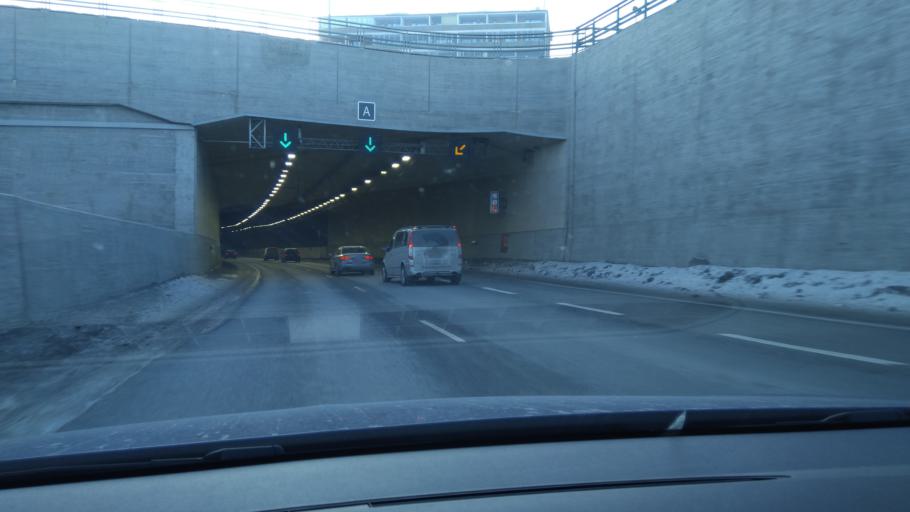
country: FI
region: Pirkanmaa
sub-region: Tampere
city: Tampere
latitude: 61.5016
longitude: 23.7311
